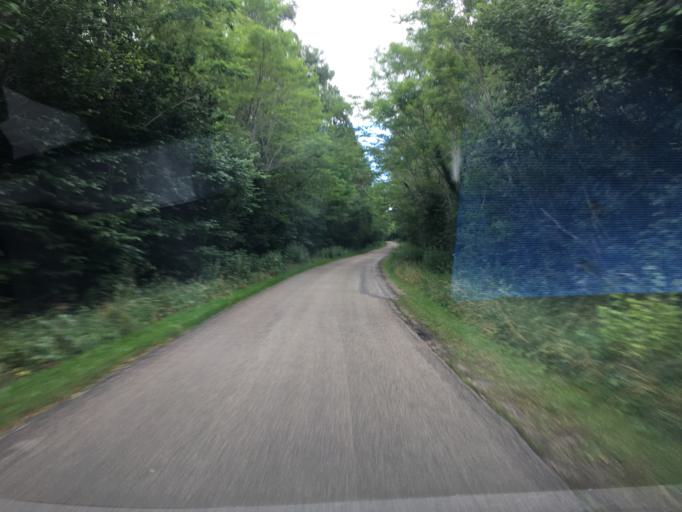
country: FR
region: Bourgogne
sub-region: Departement de l'Yonne
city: Fleury-la-Vallee
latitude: 47.8604
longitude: 3.4845
